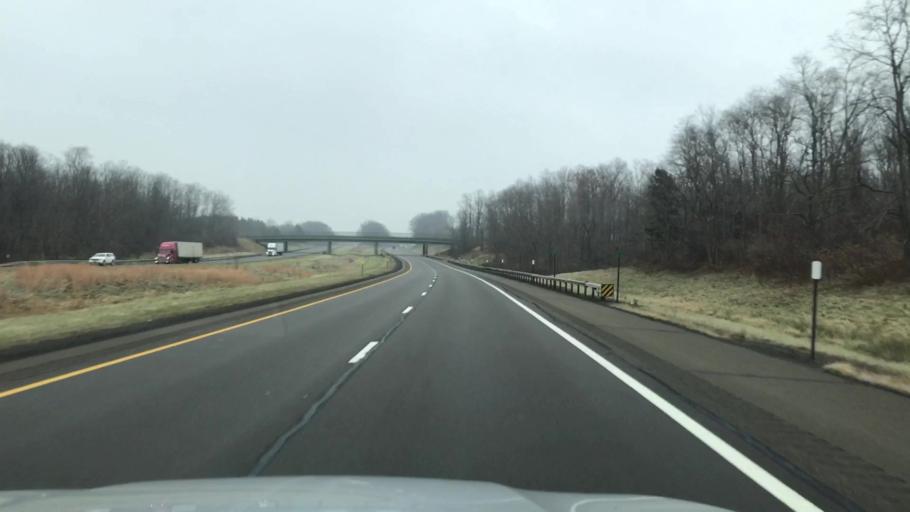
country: US
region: New York
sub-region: Chautauqua County
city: Brocton
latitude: 42.4195
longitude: -79.4021
